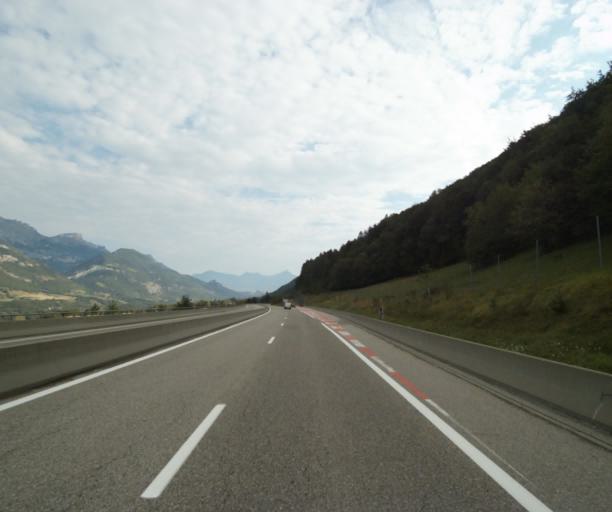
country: FR
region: Rhone-Alpes
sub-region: Departement de l'Isere
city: Le Gua
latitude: 44.9847
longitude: 5.6481
